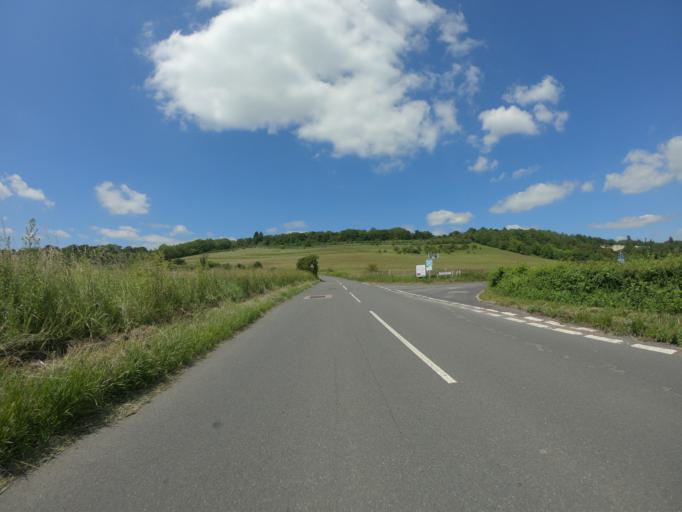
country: GB
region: England
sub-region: Kent
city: Halstead
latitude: 51.3058
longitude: 0.1507
